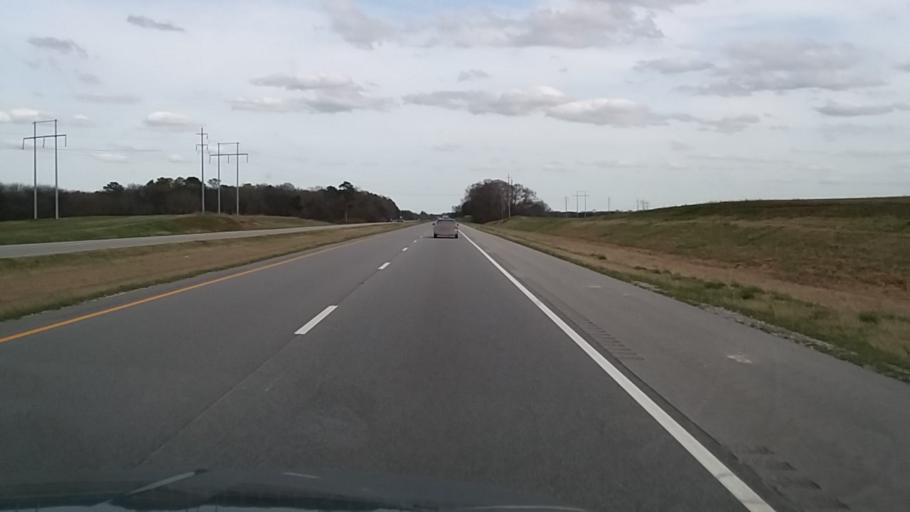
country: US
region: Alabama
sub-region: Lawrence County
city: Town Creek
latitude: 34.6825
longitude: -87.4712
